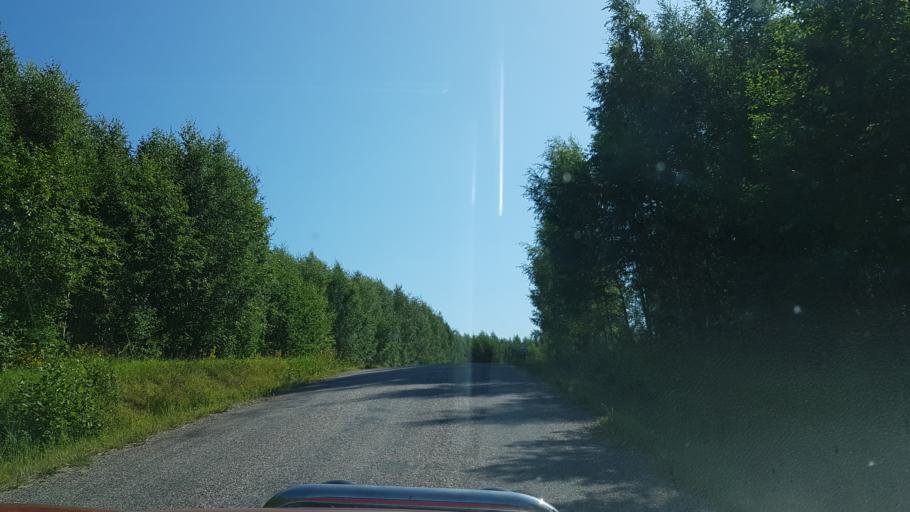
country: EE
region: Vorumaa
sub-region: Voru linn
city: Voru
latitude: 57.7187
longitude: 27.1132
